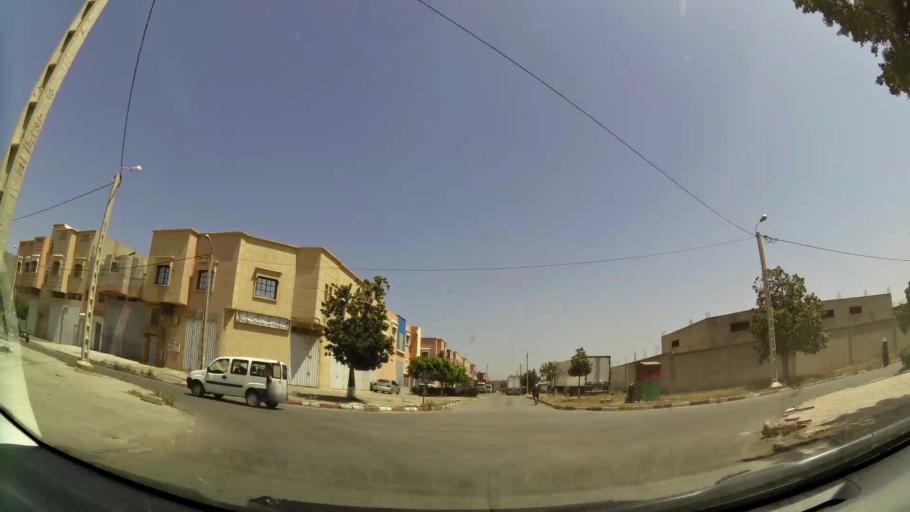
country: MA
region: Souss-Massa-Draa
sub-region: Inezgane-Ait Mellou
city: Inezgane
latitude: 30.3293
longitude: -9.4931
